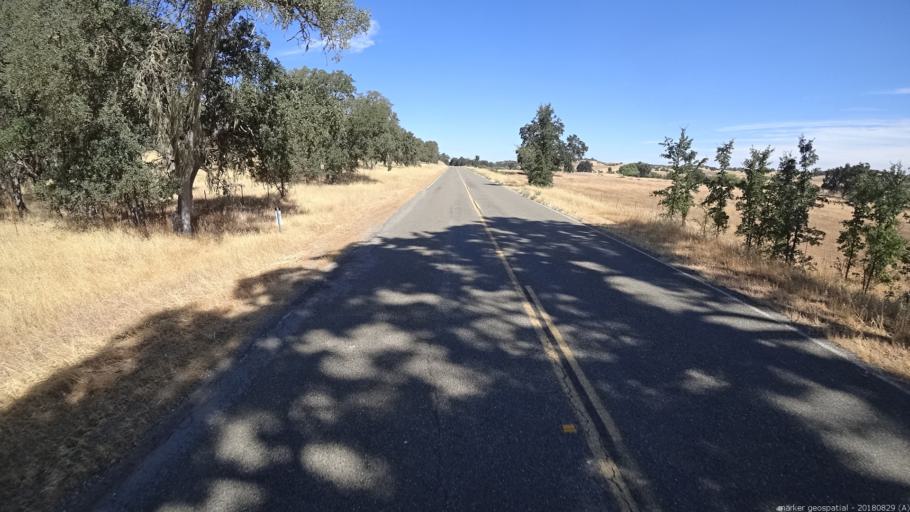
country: US
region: California
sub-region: San Luis Obispo County
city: Lake Nacimiento
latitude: 35.8164
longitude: -121.0076
